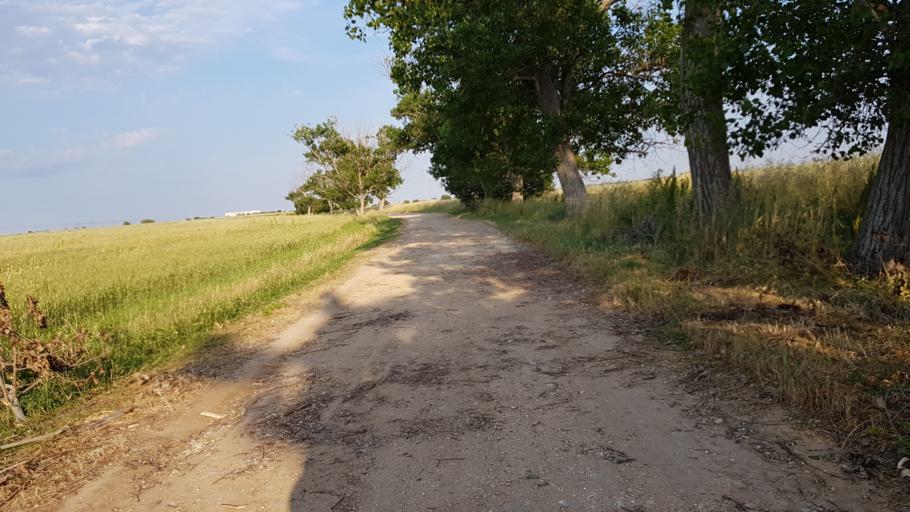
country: IT
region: Apulia
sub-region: Provincia di Brindisi
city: Brindisi
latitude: 40.6270
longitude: 17.8679
